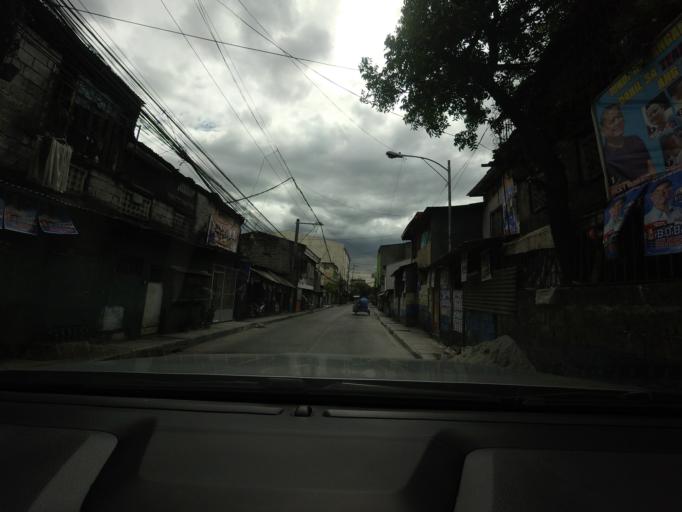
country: PH
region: Calabarzon
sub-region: Province of Rizal
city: Pateros
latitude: 14.5627
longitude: 121.0882
